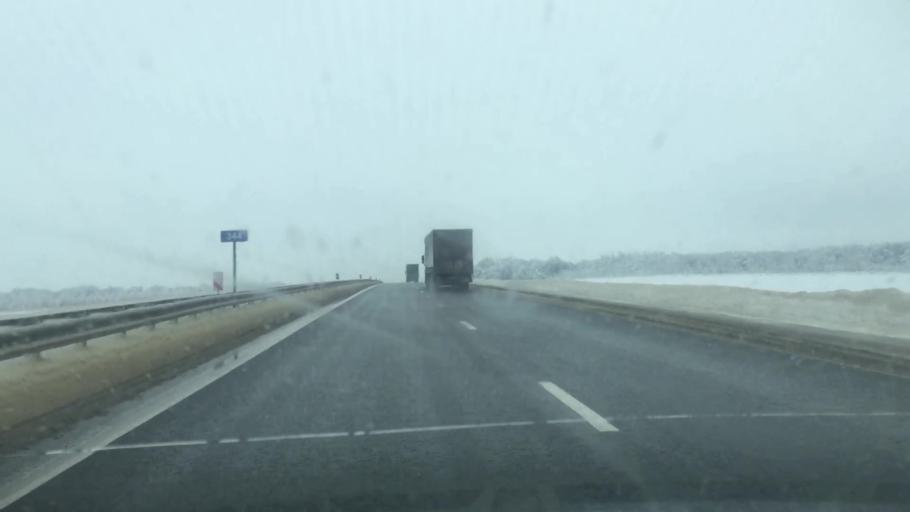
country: RU
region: Lipetsk
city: Stanovoye
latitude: 52.8952
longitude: 38.2310
